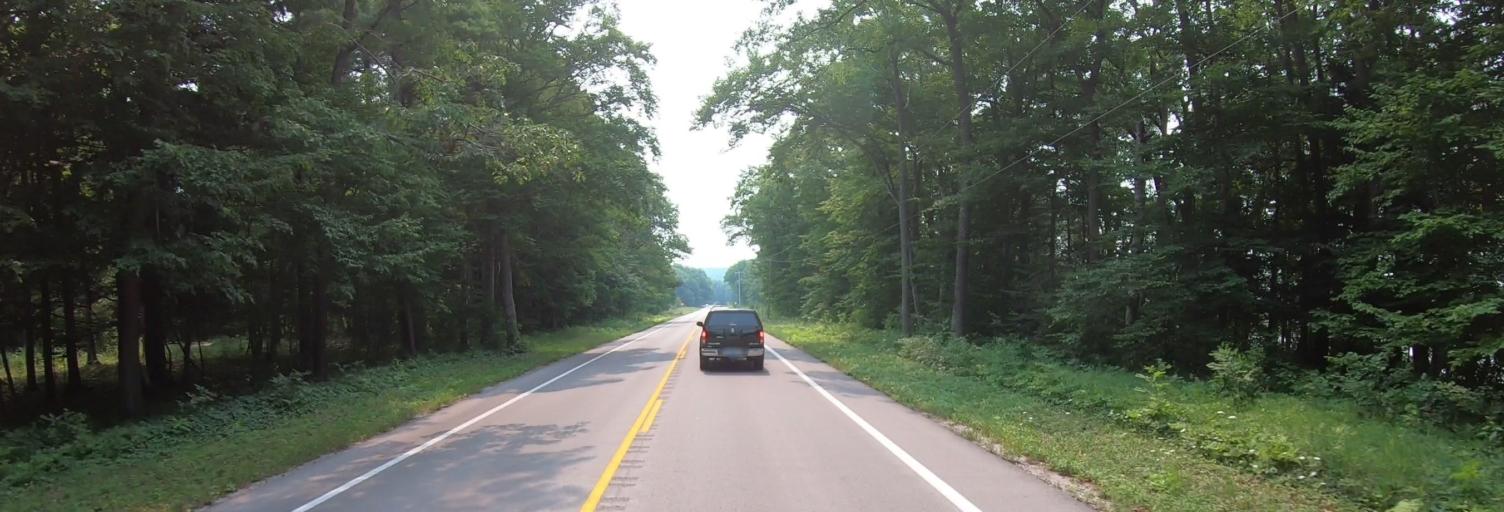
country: US
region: Michigan
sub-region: Leelanau County
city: Leland
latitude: 44.9274
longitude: -85.8829
